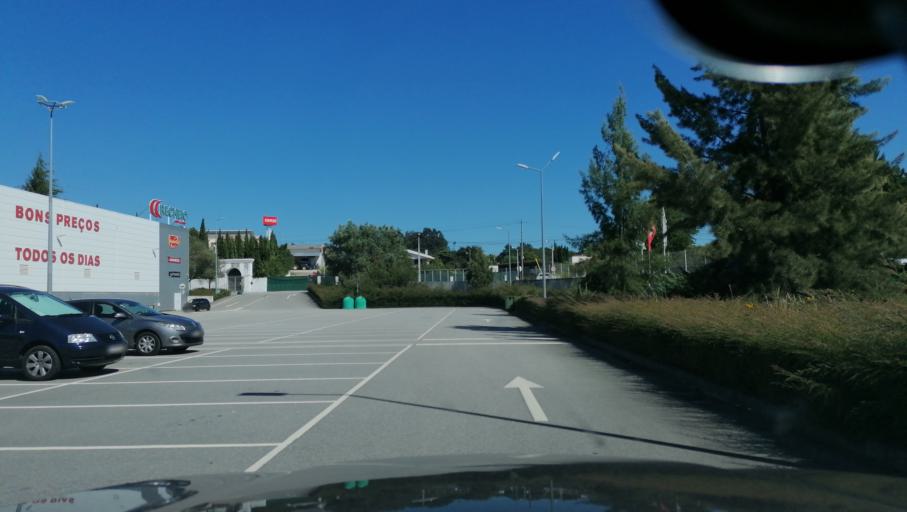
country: PT
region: Aveiro
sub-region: Santa Maria da Feira
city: Feira
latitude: 40.9318
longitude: -8.5275
